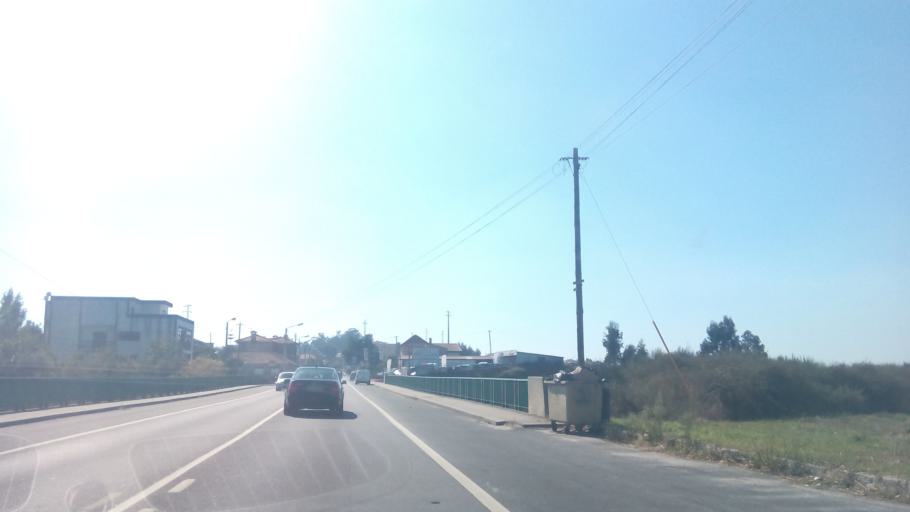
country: PT
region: Porto
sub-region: Penafiel
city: Penafiel
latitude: 41.2201
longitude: -8.2589
